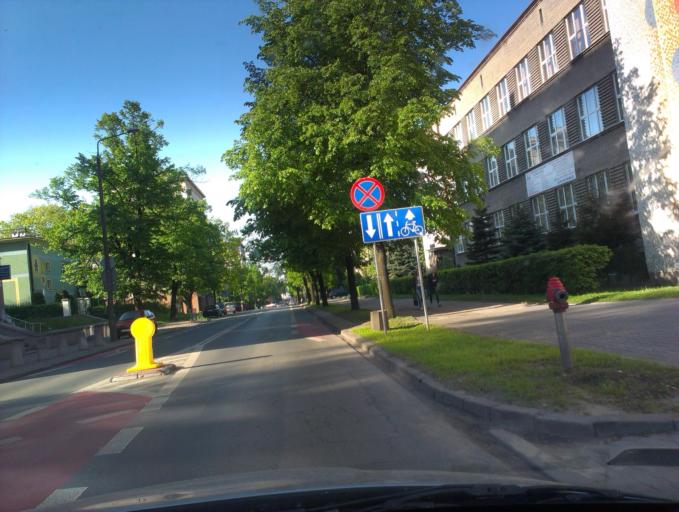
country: PL
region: Masovian Voivodeship
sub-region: Radom
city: Radom
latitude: 51.3958
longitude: 21.1507
